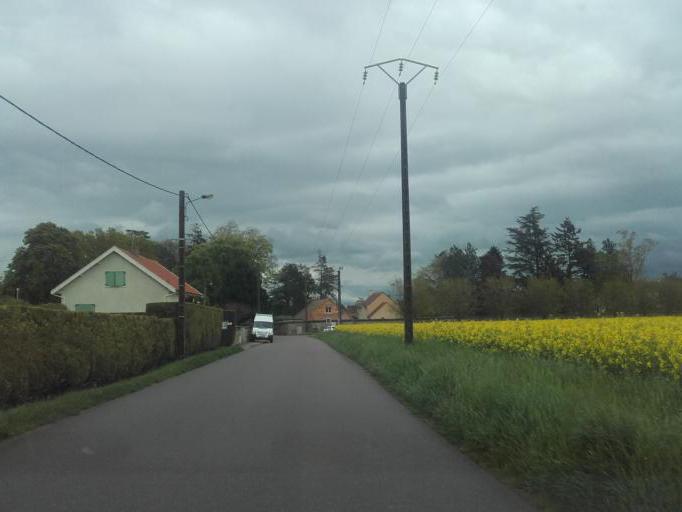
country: FR
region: Bourgogne
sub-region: Departement de la Cote-d'Or
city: Beaune
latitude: 47.0482
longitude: 4.8622
